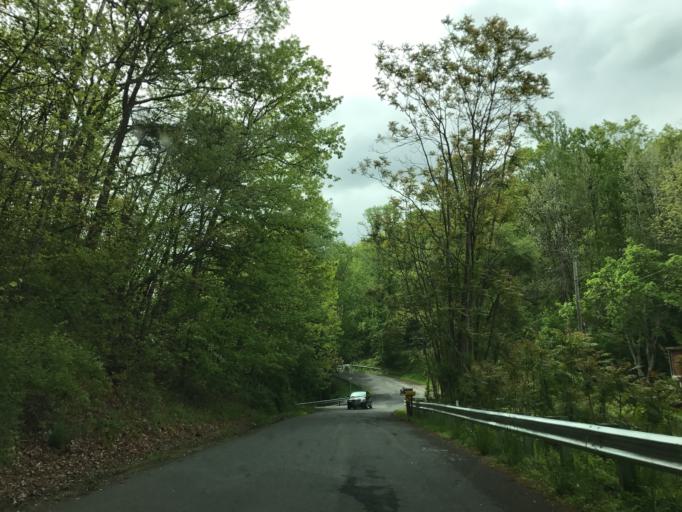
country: US
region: Maryland
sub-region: Carroll County
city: Hampstead
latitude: 39.5403
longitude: -76.8996
